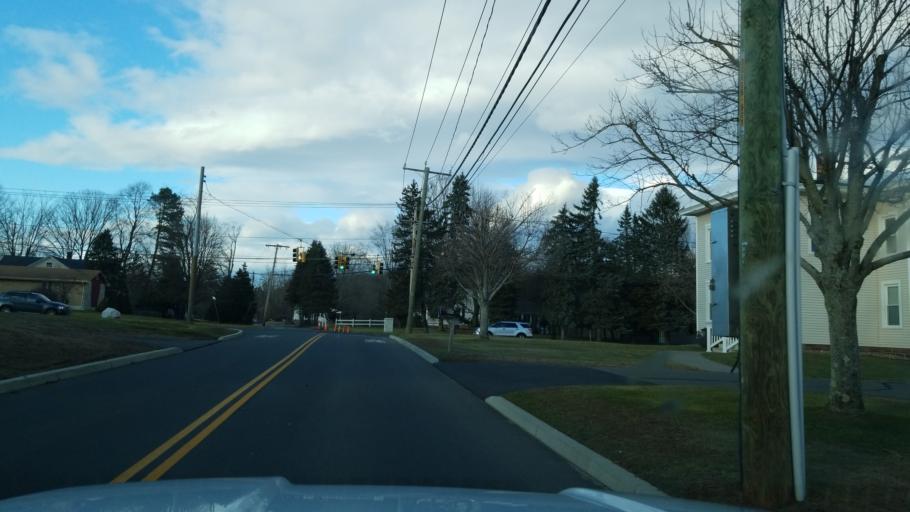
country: US
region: Connecticut
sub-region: Middlesex County
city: Middletown
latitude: 41.5330
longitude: -72.6337
